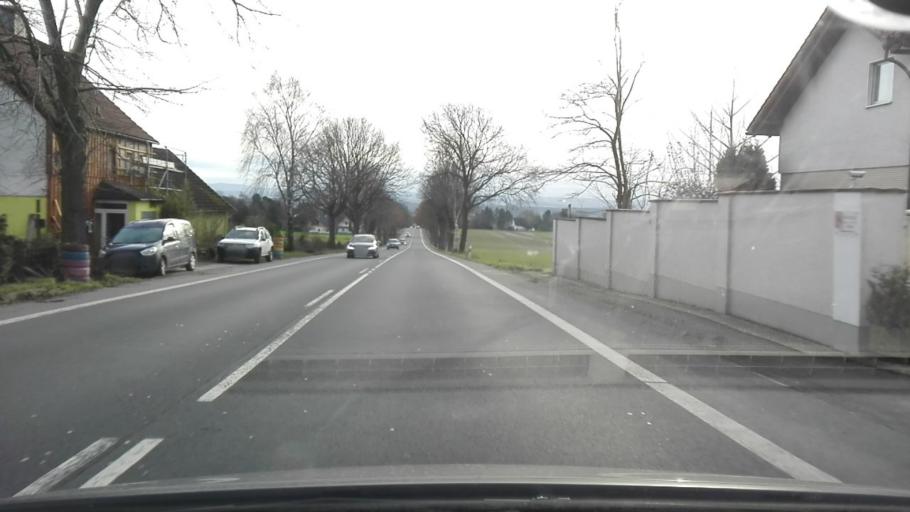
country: DE
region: North Rhine-Westphalia
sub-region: Regierungsbezirk Arnsberg
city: Unna
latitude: 51.4960
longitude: 7.7047
